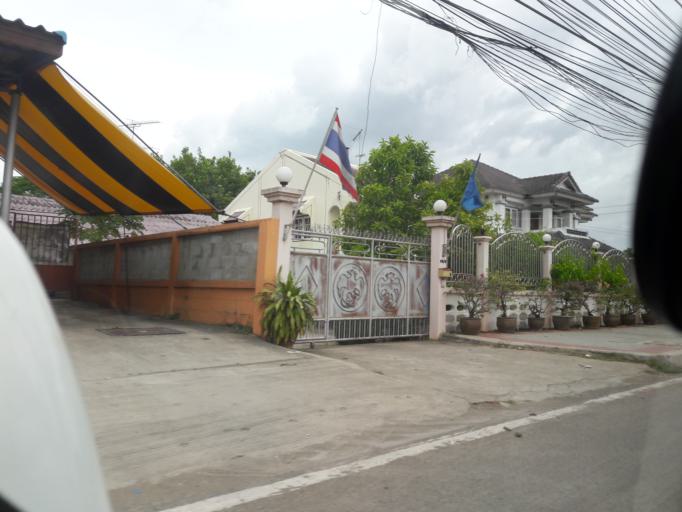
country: TH
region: Ratchaburi
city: Damnoen Saduak
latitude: 13.5906
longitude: 99.9641
